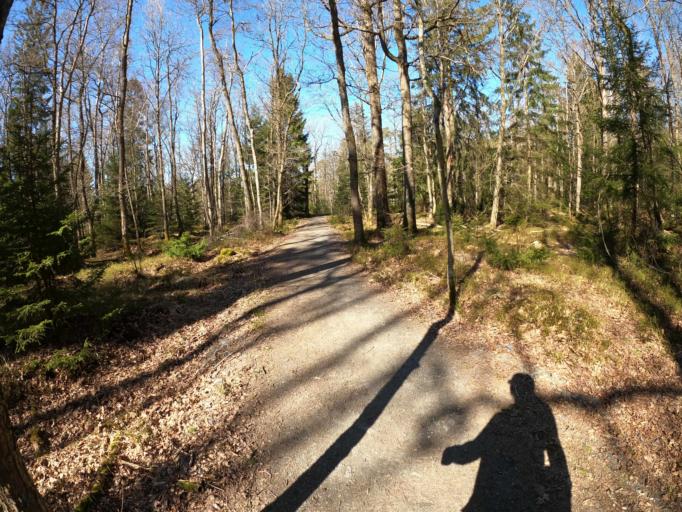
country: SE
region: Vaestra Goetaland
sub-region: Harryda Kommun
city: Molnlycke
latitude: 57.6250
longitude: 12.1123
